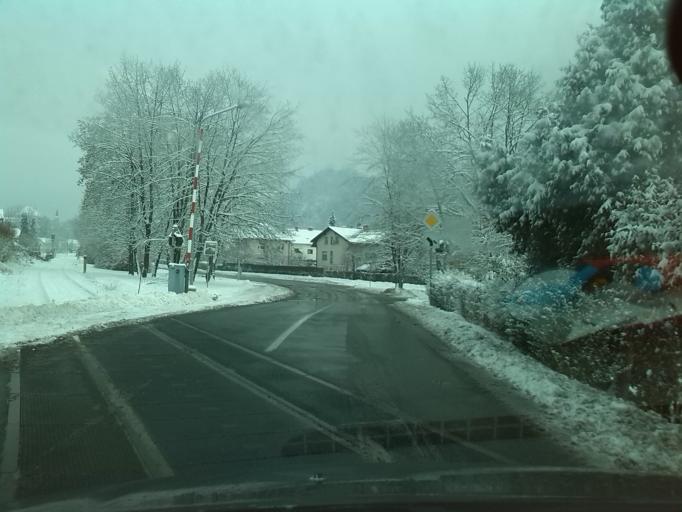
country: SI
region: Kamnik
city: Kamnik
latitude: 46.2179
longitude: 14.5999
